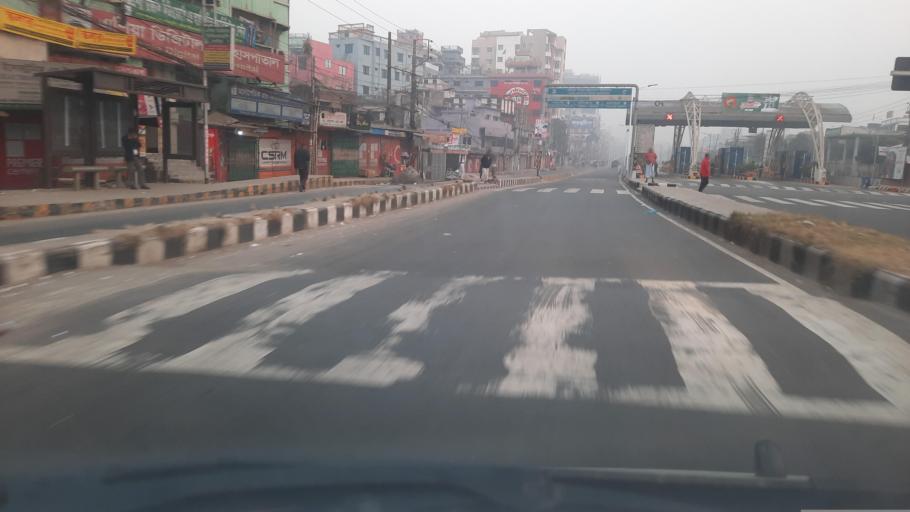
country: BD
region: Dhaka
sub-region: Dhaka
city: Dhaka
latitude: 23.7037
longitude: 90.4351
